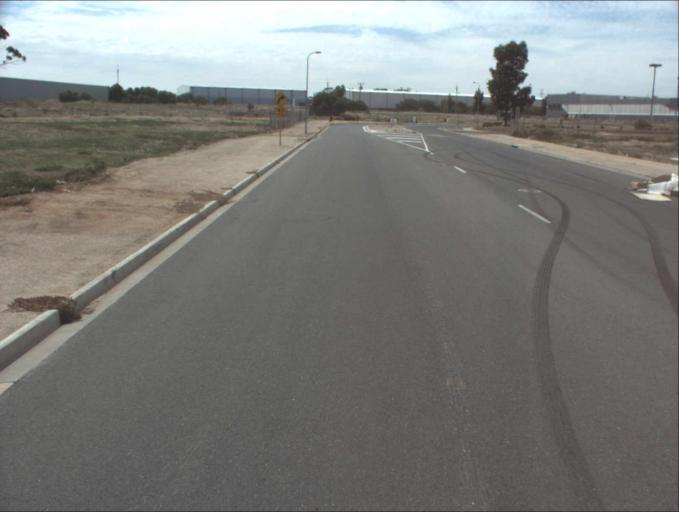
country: AU
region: South Australia
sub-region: Port Adelaide Enfield
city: Enfield
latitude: -34.8377
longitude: 138.6019
